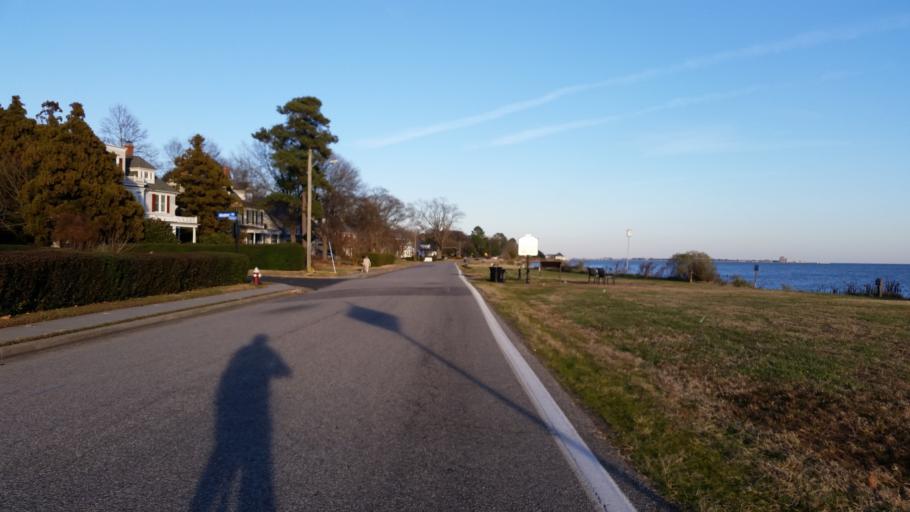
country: US
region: Virginia
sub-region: City of Hampton
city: Hampton
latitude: 37.0006
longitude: -76.3680
